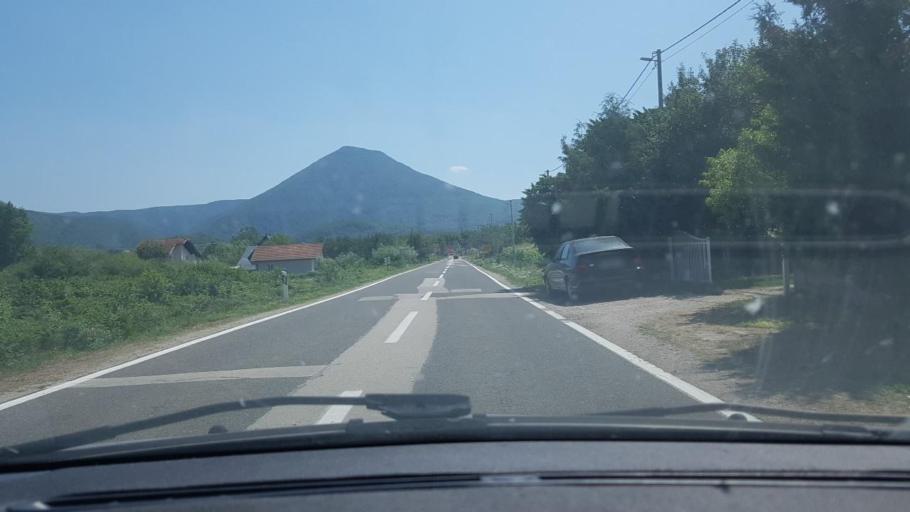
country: BA
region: Federation of Bosnia and Herzegovina
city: Bihac
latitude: 44.7679
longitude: 15.9443
